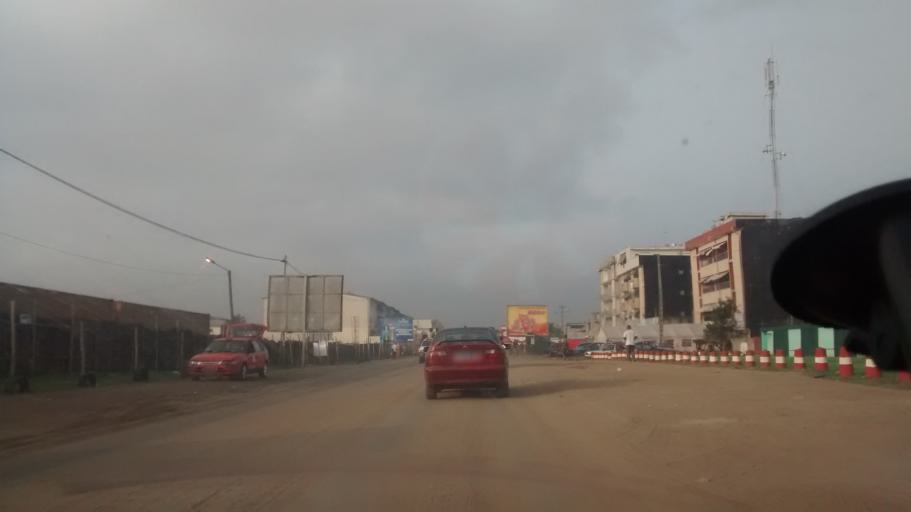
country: CI
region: Lagunes
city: Abobo
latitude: 5.4120
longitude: -3.9821
